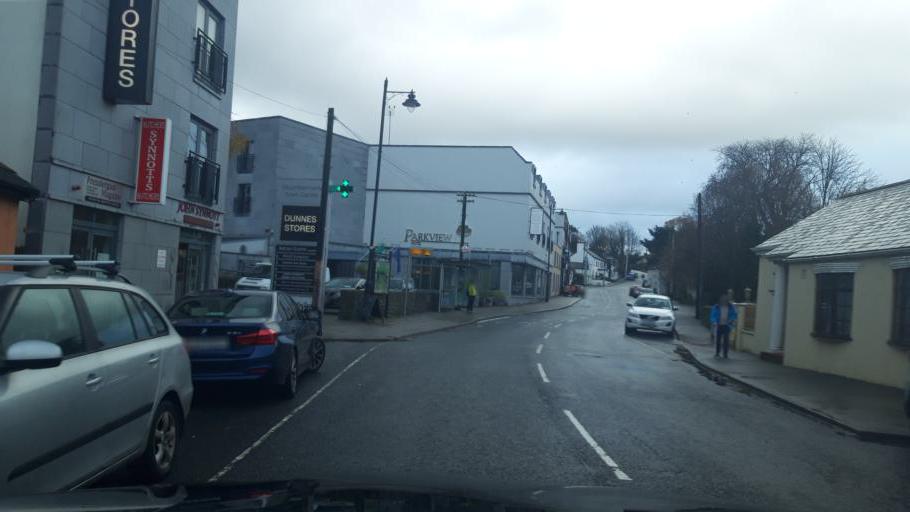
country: IE
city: Newtownmountkennedy
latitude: 53.0916
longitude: -6.1121
